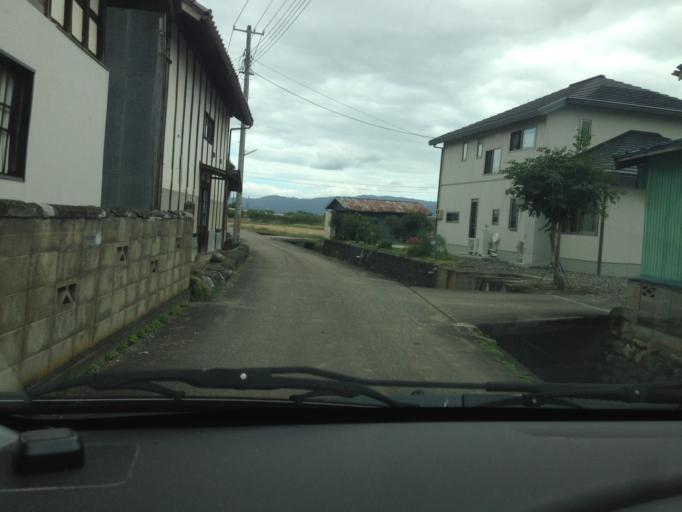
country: JP
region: Fukushima
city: Kitakata
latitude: 37.4933
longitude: 139.8315
